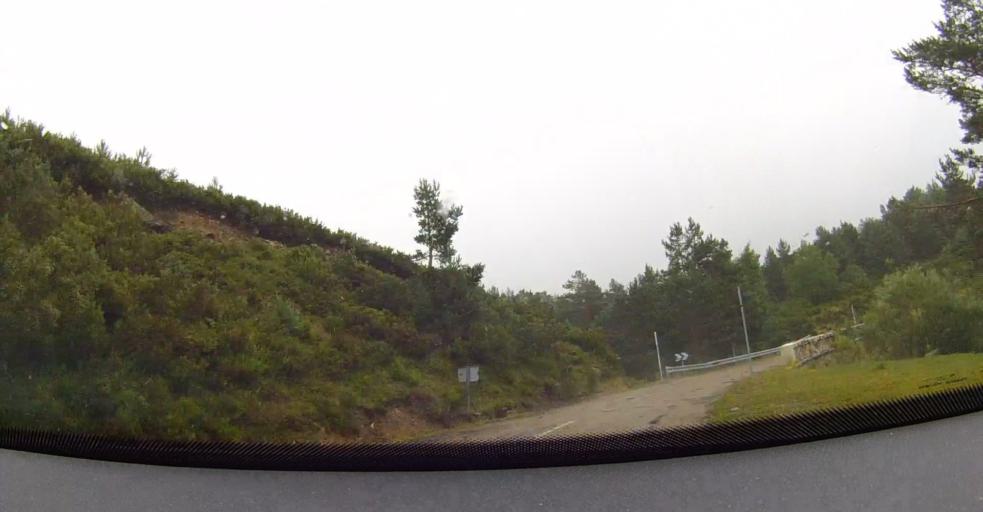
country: ES
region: Castille and Leon
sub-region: Provincia de Leon
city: Puebla de Lillo
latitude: 43.0758
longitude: -5.2471
